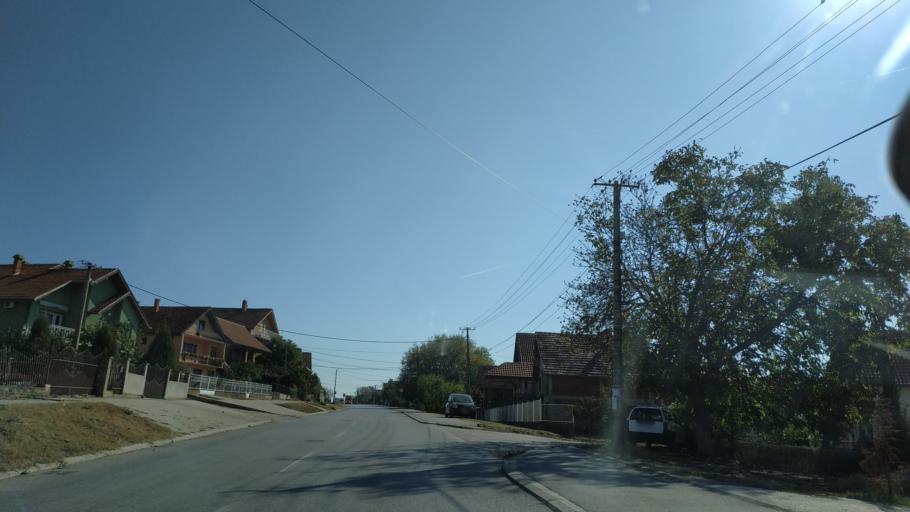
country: RS
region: Central Serbia
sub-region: Nisavski Okrug
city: Aleksinac
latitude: 43.5471
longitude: 21.6937
